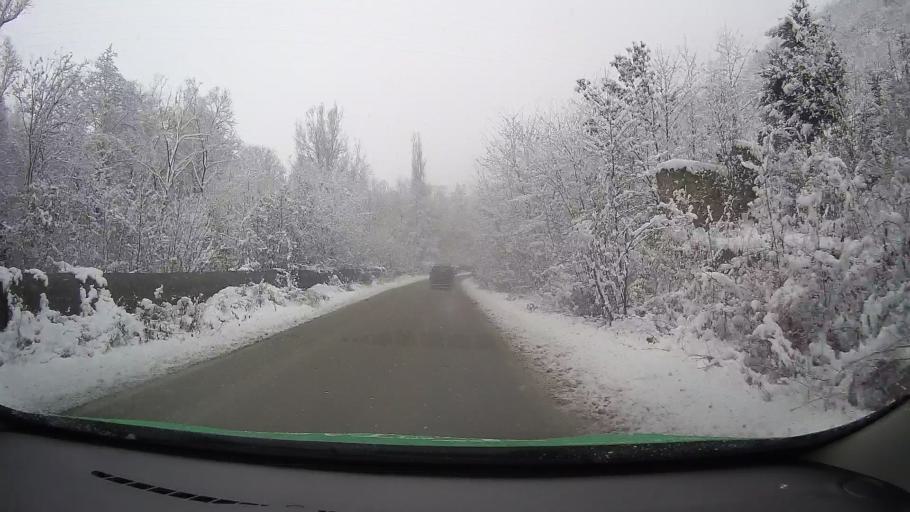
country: RO
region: Hunedoara
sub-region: Comuna Teliucu Inferior
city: Teliucu Inferior
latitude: 45.7281
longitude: 22.8807
